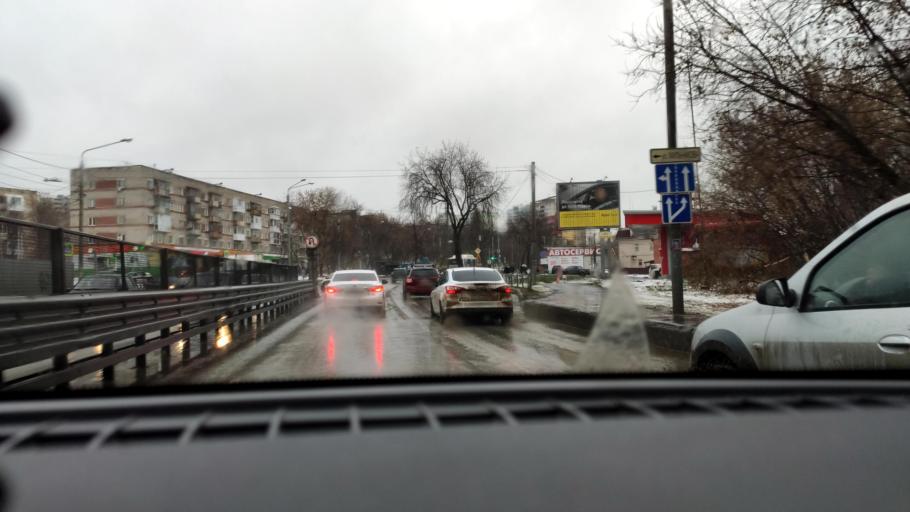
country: RU
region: Perm
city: Perm
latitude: 57.9986
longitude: 56.2251
